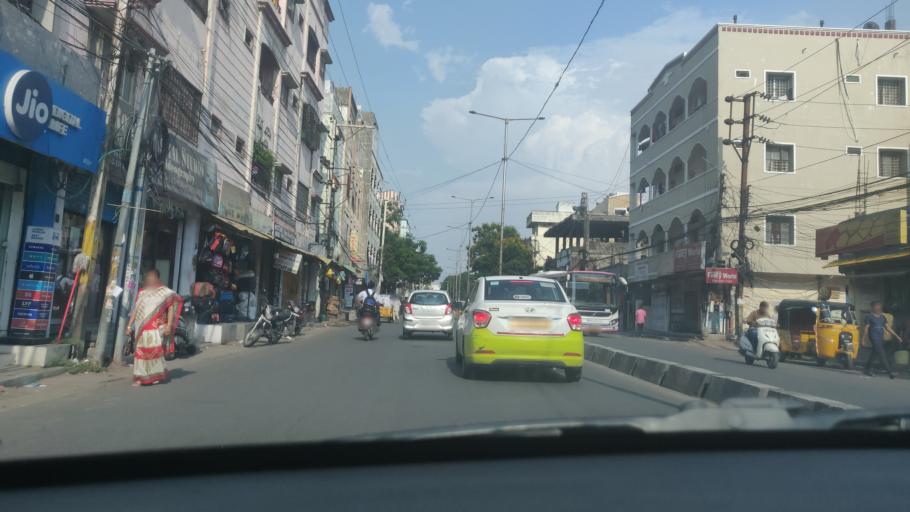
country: IN
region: Telangana
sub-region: Rangareddi
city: Gaddi Annaram
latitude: 17.3945
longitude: 78.5056
